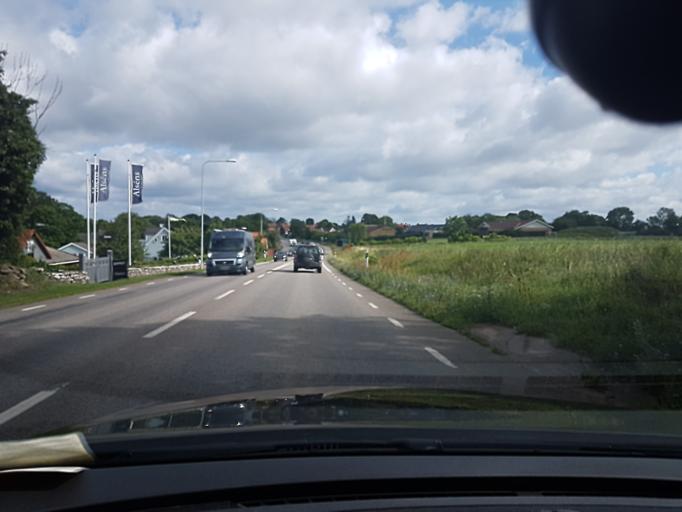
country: SE
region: Kalmar
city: Faerjestaden
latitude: 56.7159
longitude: 16.5341
